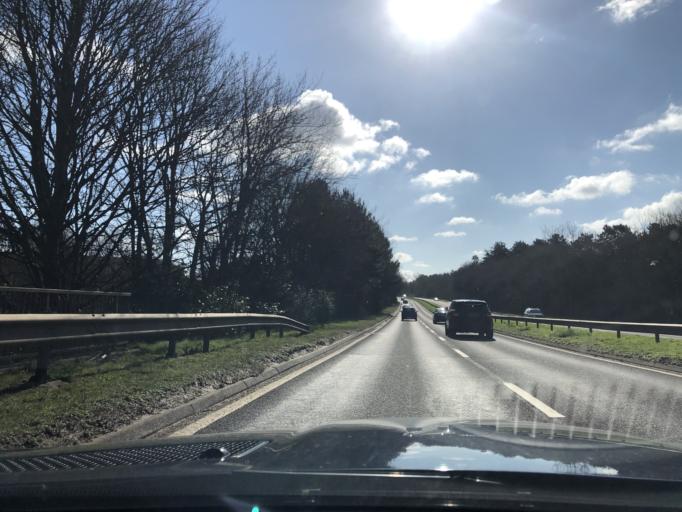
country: GB
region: England
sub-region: Northamptonshire
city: Northampton
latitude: 52.2607
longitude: -0.8405
